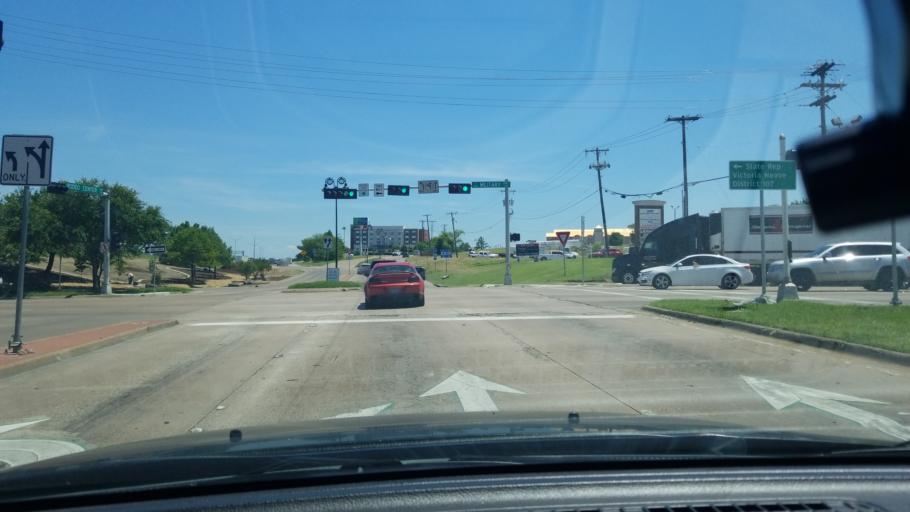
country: US
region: Texas
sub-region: Dallas County
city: Mesquite
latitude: 32.7681
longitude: -96.6231
